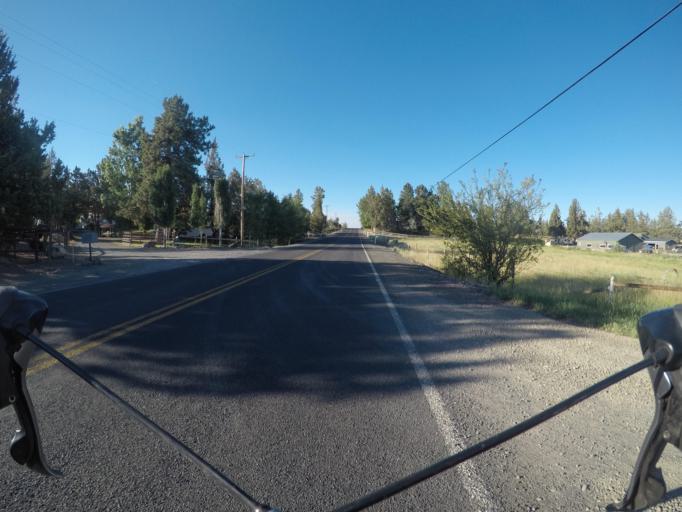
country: US
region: Oregon
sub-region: Deschutes County
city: Redmond
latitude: 44.2559
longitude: -121.2396
